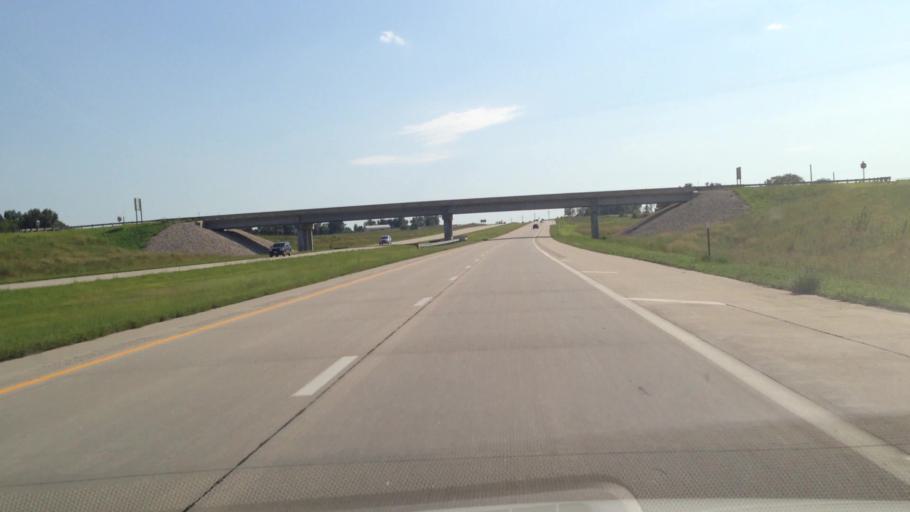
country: US
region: Kansas
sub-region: Linn County
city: Pleasanton
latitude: 38.2194
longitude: -94.7004
